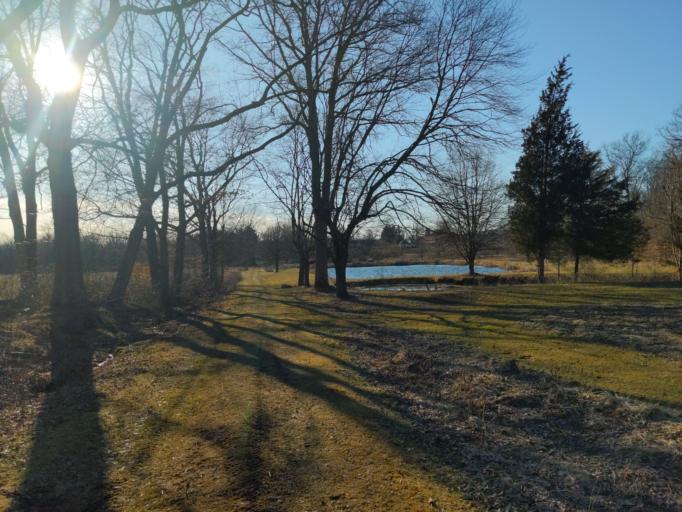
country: US
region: Pennsylvania
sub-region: Bucks County
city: Spinnerstown
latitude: 40.4432
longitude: -75.3938
